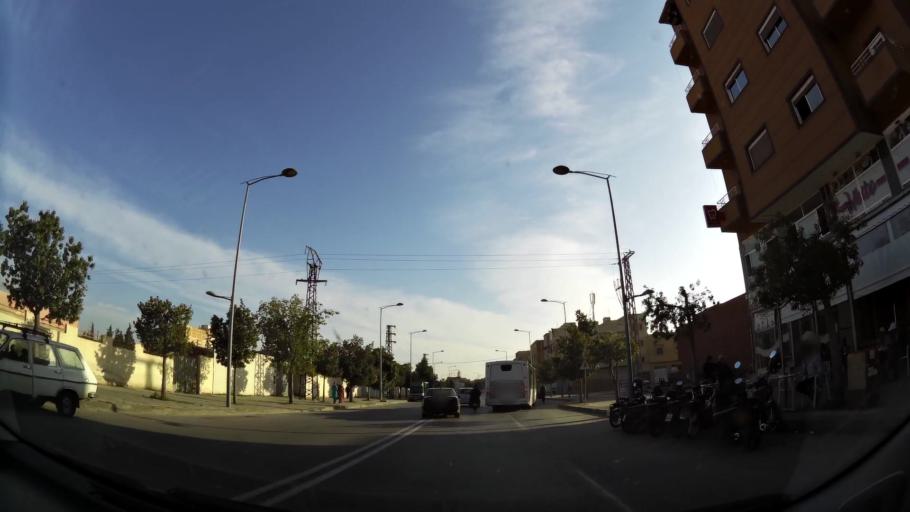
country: MA
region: Oriental
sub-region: Oujda-Angad
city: Oujda
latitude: 34.7058
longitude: -1.8941
